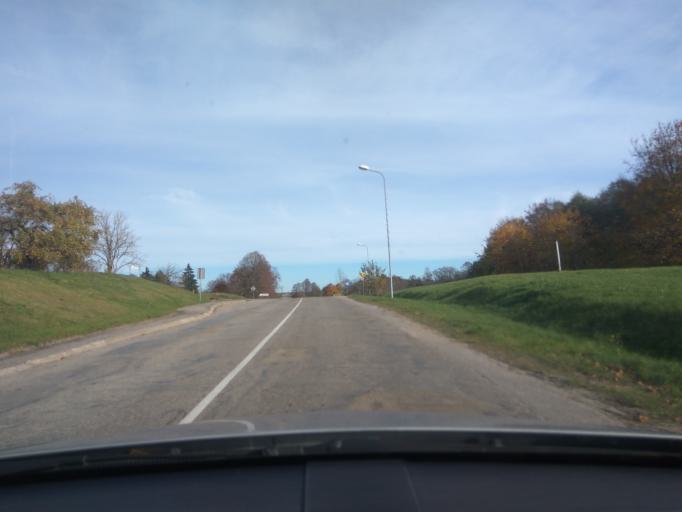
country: LV
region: Alsunga
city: Alsunga
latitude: 56.9835
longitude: 21.5718
